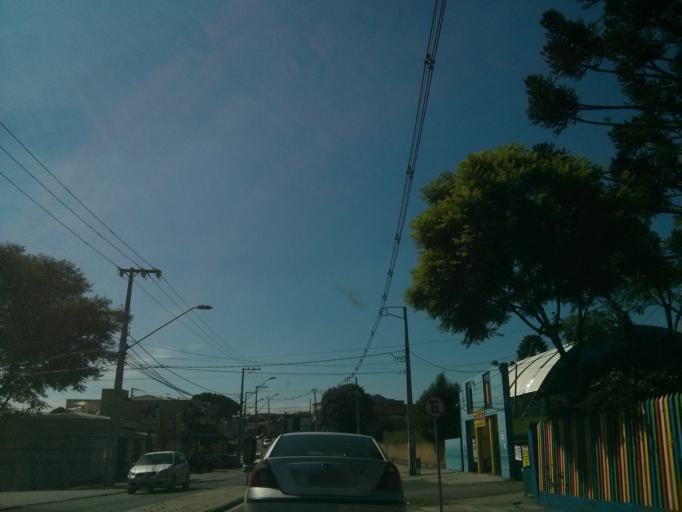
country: BR
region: Parana
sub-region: Sao Jose Dos Pinhais
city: Sao Jose dos Pinhais
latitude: -25.5498
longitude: -49.1961
